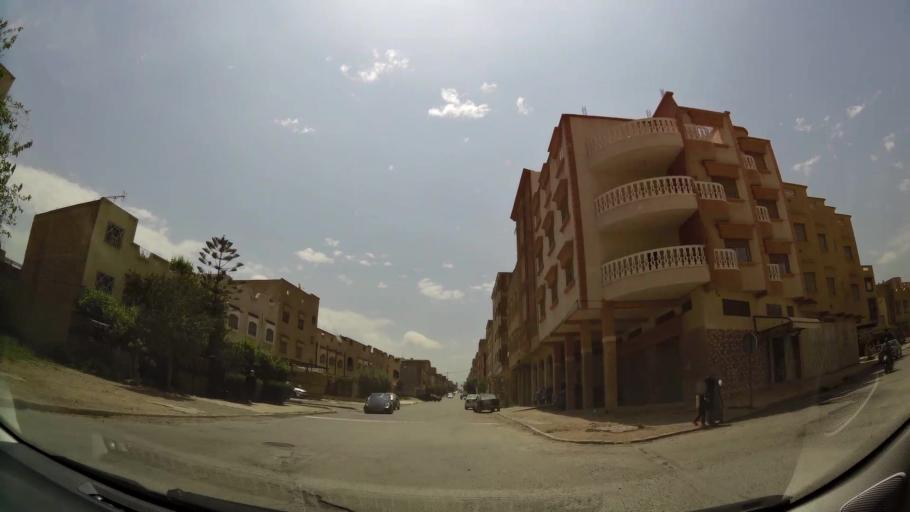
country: MA
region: Oriental
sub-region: Oujda-Angad
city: Oujda
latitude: 34.6894
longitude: -1.8859
